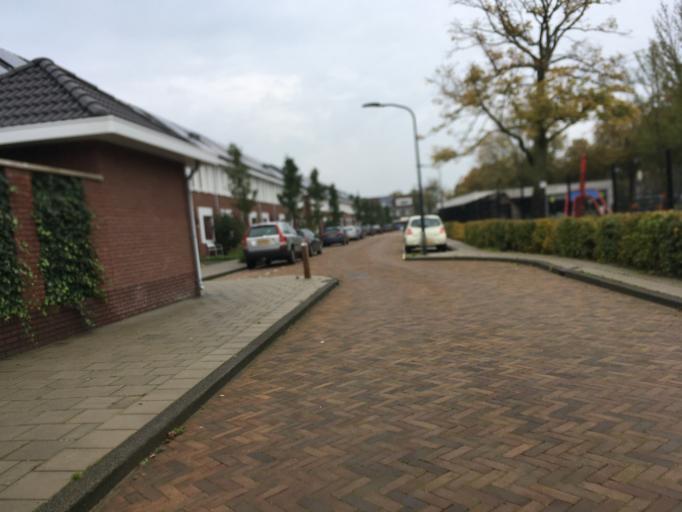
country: NL
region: North Holland
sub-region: Gemeente Haarlem
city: Haarlem
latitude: 52.3771
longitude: 4.6572
